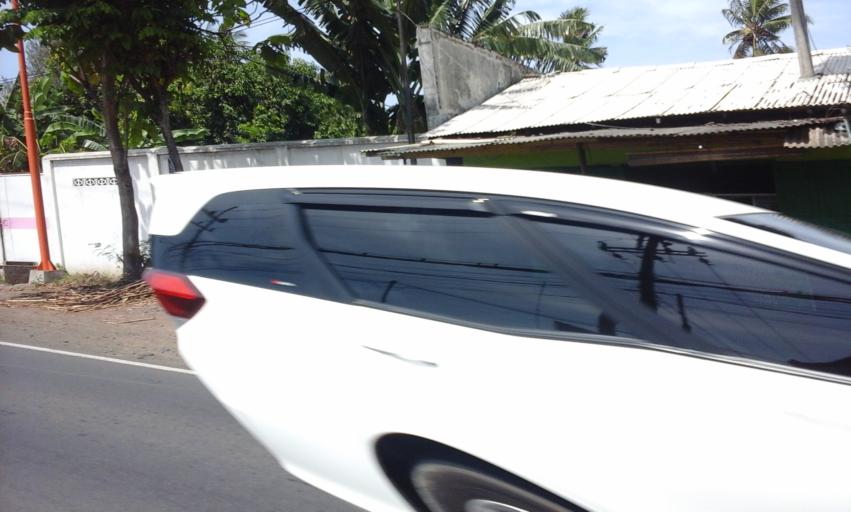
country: ID
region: East Java
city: Klatakan
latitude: -8.1766
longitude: 114.3834
